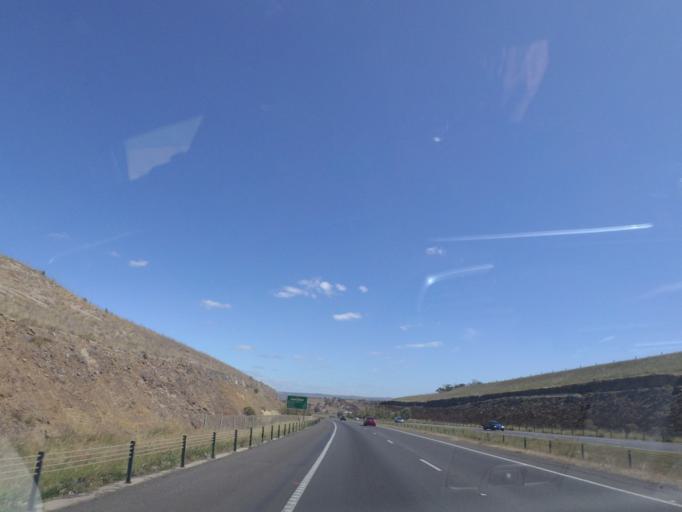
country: AU
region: Victoria
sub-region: Melton
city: Brookfield
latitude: -37.6862
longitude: 144.4998
